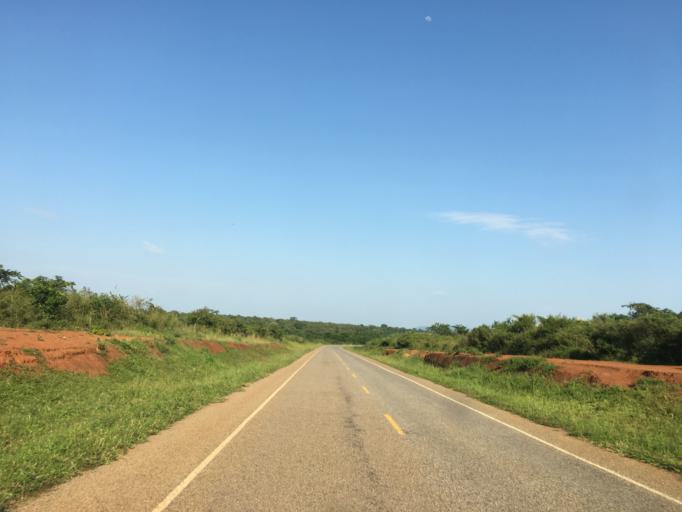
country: UG
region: Western Region
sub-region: Kiryandongo District
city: Masindi Port
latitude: 1.5850
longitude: 31.9146
